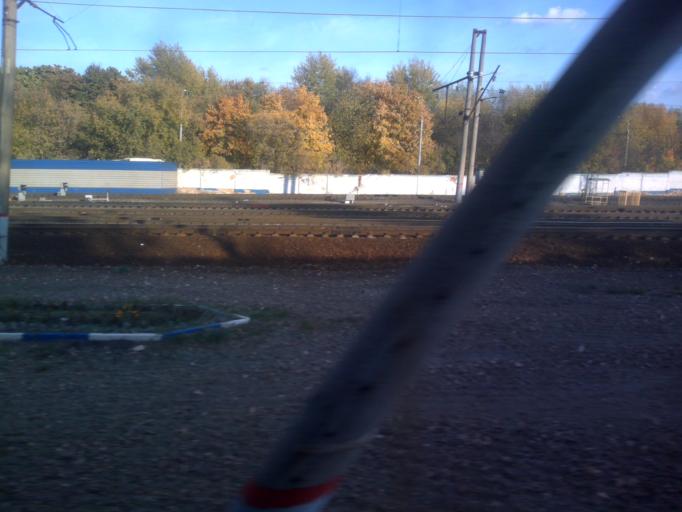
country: RU
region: Moscow
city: Tekstil'shchiki
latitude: 55.6834
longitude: 37.7327
